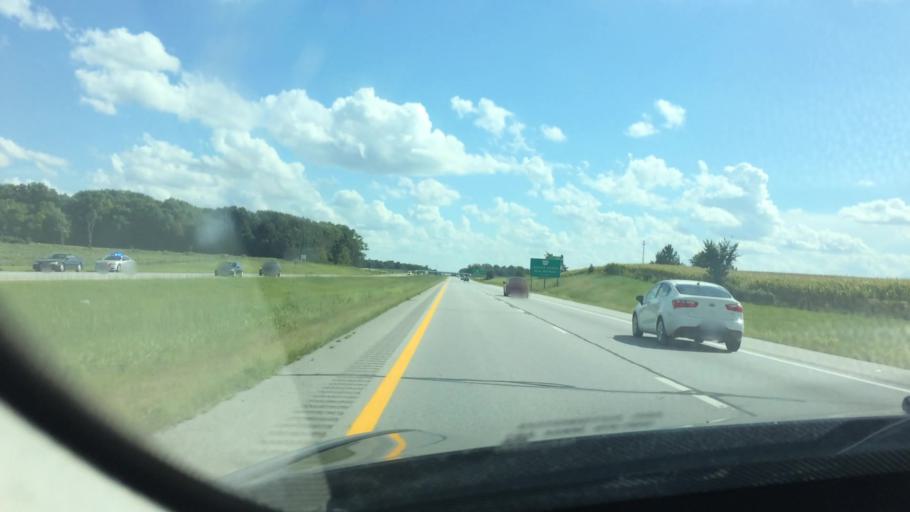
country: US
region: Ohio
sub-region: Shelby County
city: Botkins
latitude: 40.4487
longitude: -84.1696
